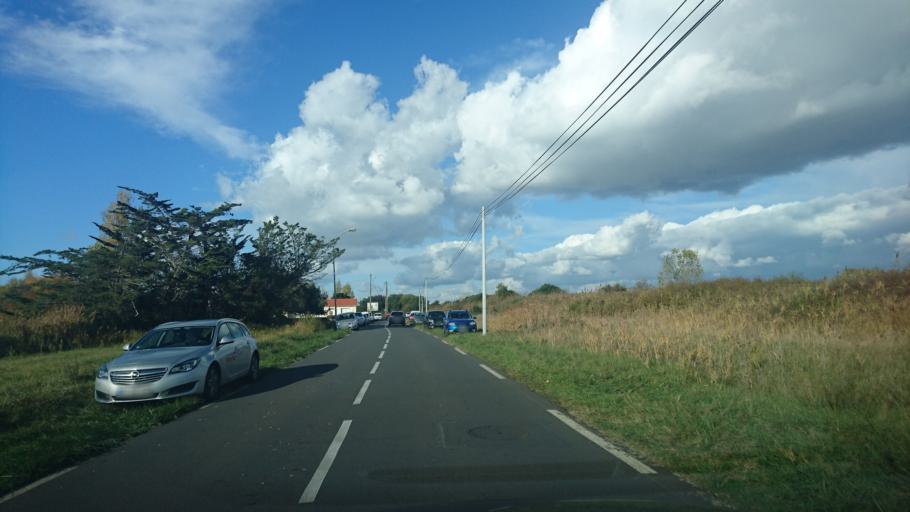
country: FR
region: Pays de la Loire
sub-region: Departement de la Vendee
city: Les Sables-d'Olonne
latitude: 46.5117
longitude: -1.8038
